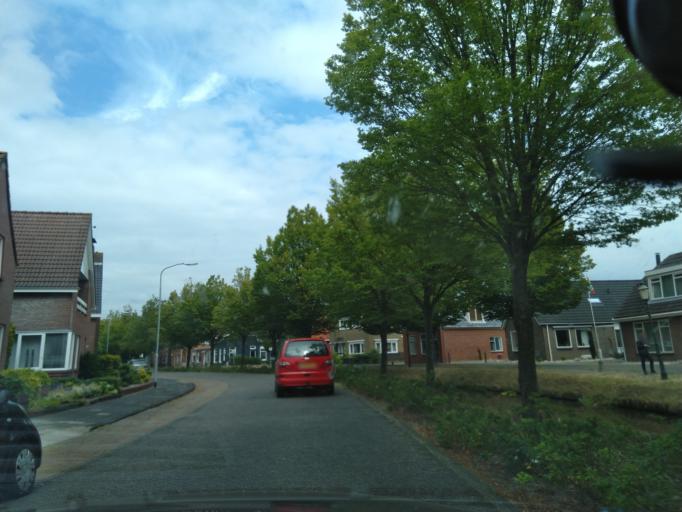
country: NL
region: Groningen
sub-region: Gemeente Pekela
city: Oude Pekela
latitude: 53.1009
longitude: 7.0056
